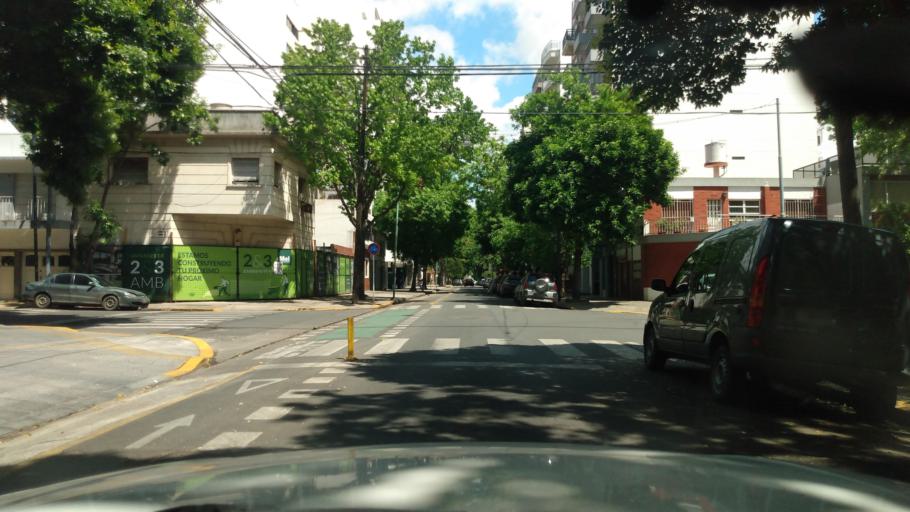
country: AR
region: Buenos Aires F.D.
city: Villa Santa Rita
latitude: -34.5783
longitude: -58.4911
